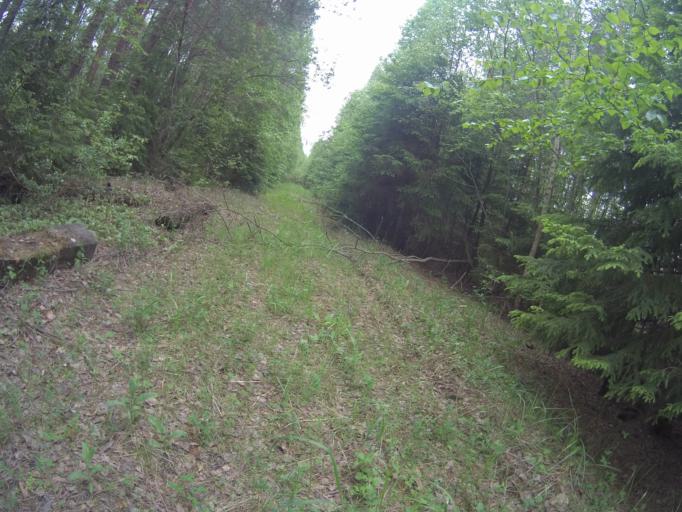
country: RU
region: Vladimir
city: Raduzhnyy
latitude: 55.9703
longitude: 40.2591
